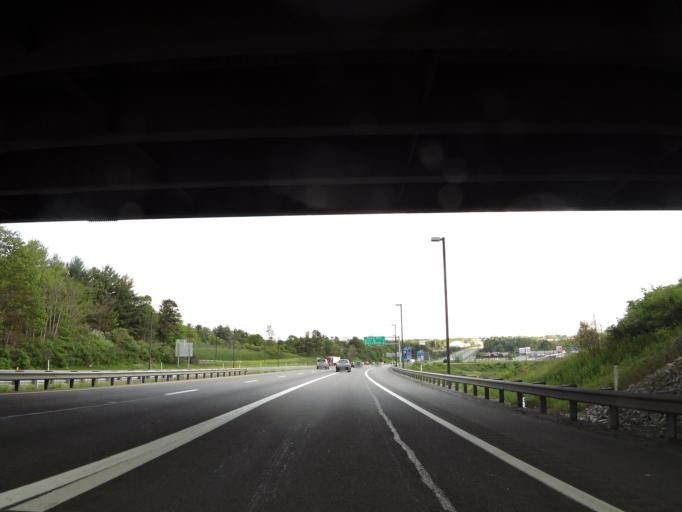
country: US
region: West Virginia
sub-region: Raleigh County
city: Prosperity
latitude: 37.8105
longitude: -81.2128
